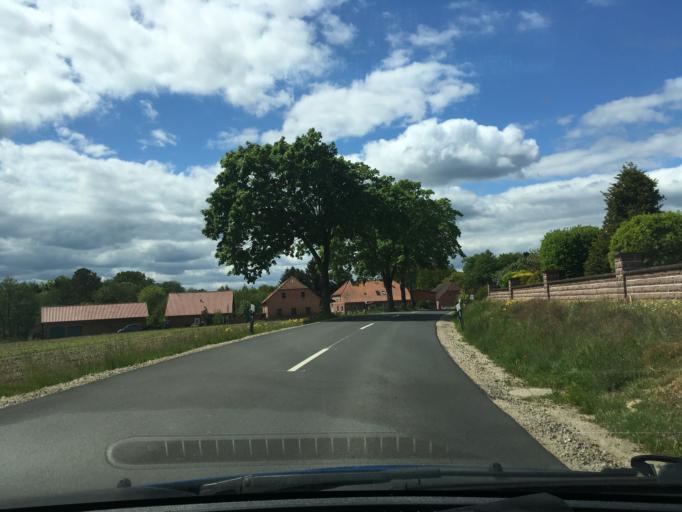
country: DE
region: Lower Saxony
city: Suderburg
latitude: 52.9128
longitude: 10.4876
